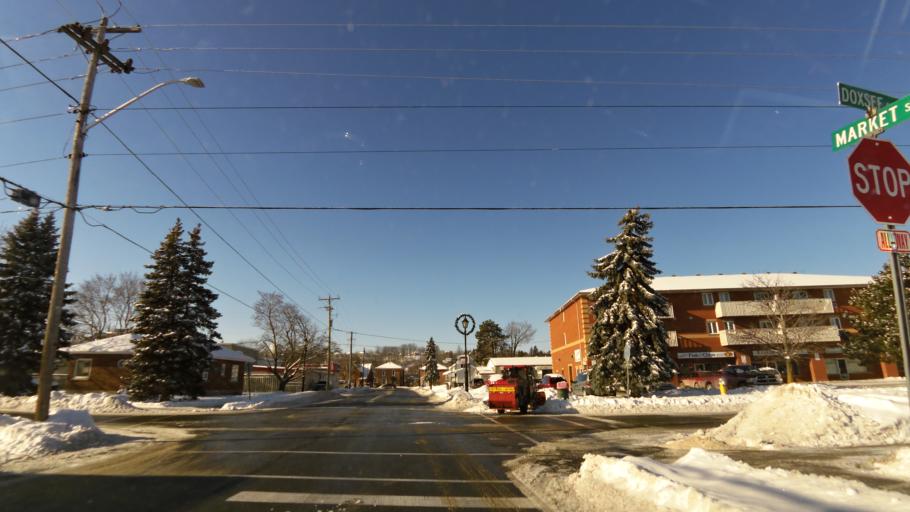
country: CA
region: Ontario
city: Quinte West
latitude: 44.3110
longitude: -77.7950
